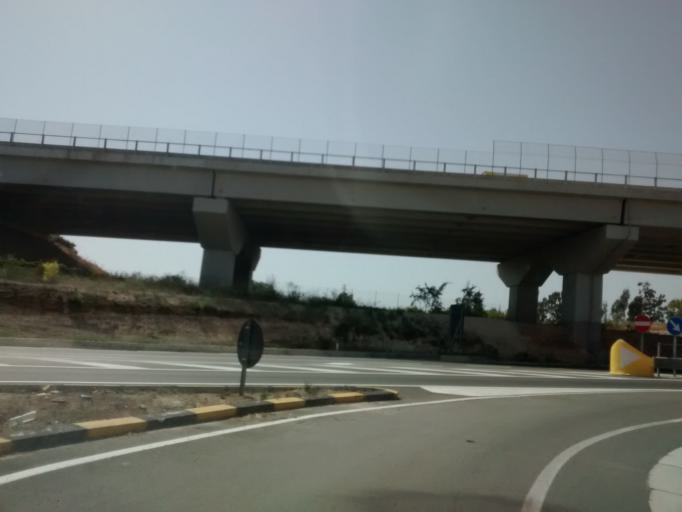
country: IT
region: Sardinia
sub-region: Provincia di Cagliari
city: Quartu Sant'Elena
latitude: 39.2593
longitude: 9.2601
